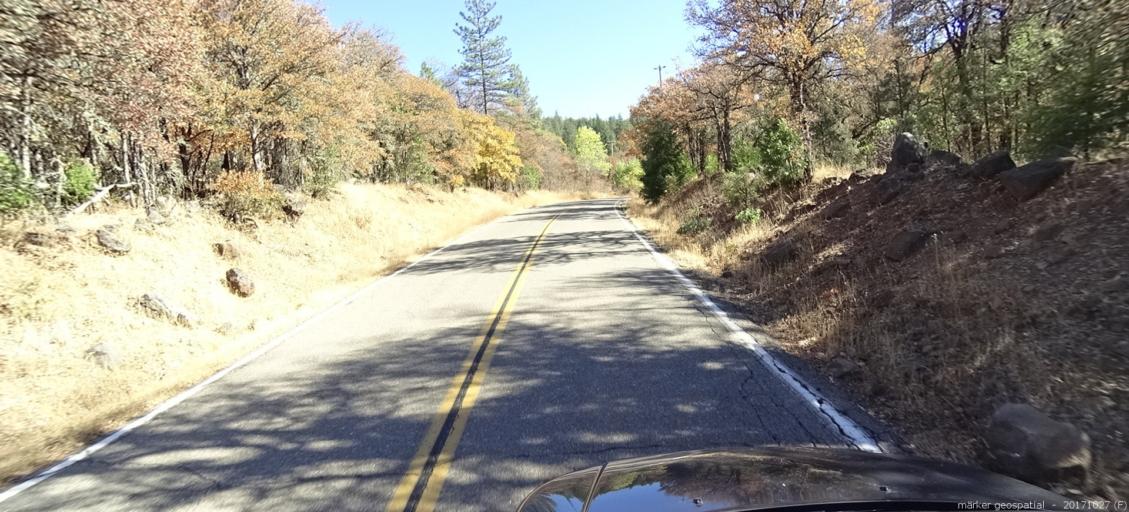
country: US
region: California
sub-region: Shasta County
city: Shingletown
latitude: 40.7032
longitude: -121.9207
